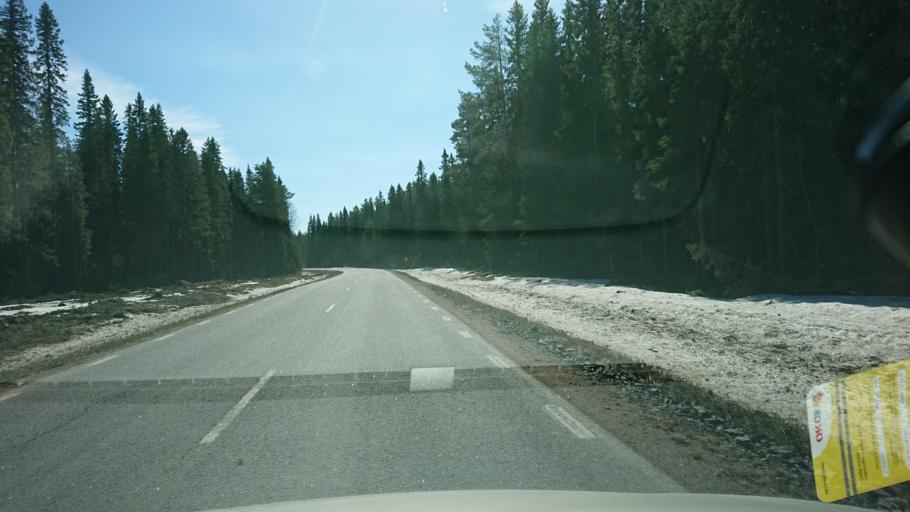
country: SE
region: Vaesternorrland
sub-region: Solleftea Kommun
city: As
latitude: 63.6690
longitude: 16.4306
